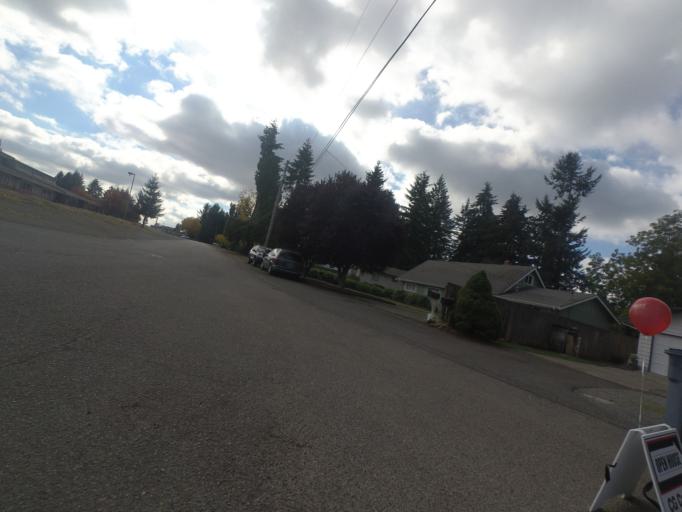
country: US
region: Washington
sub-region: Pierce County
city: University Place
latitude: 47.2188
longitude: -122.5425
